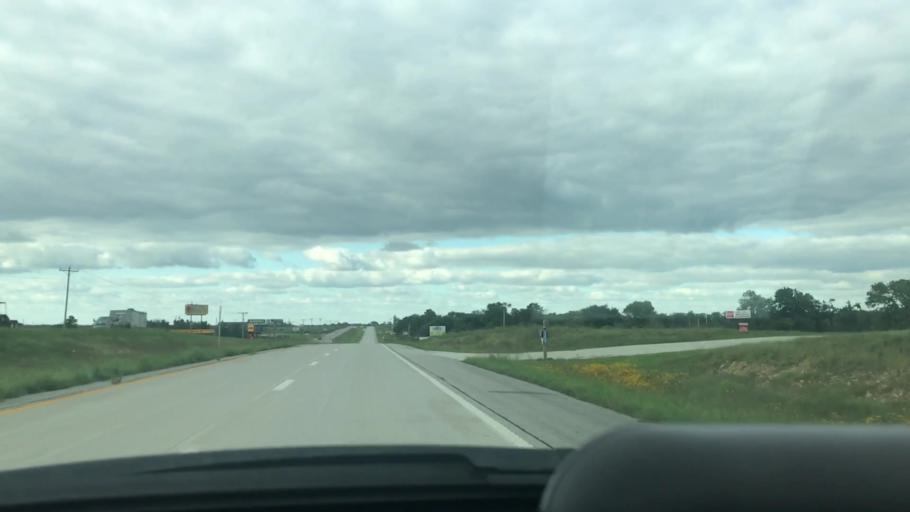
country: US
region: Missouri
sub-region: Benton County
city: Lincoln
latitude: 38.3448
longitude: -93.3402
